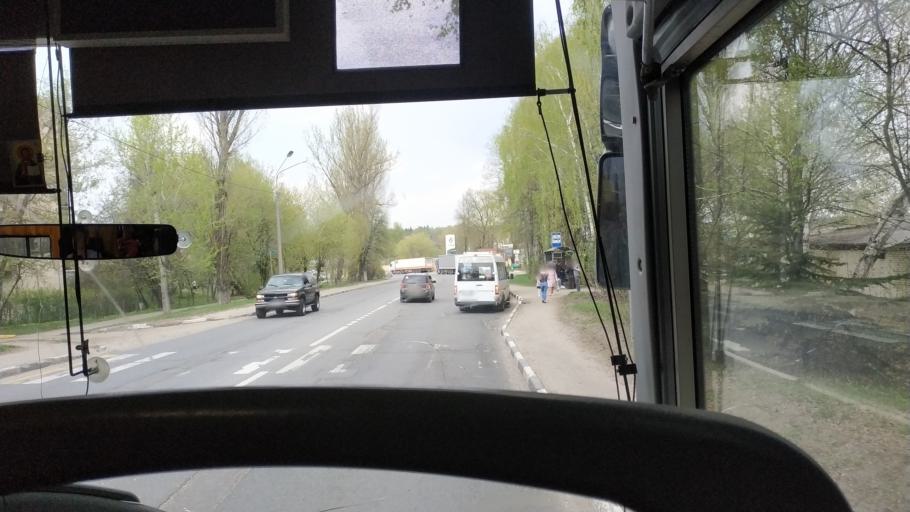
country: RU
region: Moskovskaya
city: Lytkarino
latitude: 55.5842
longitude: 37.9149
